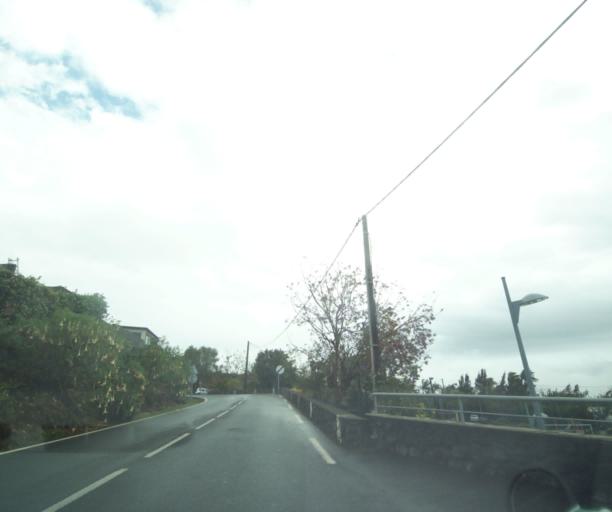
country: RE
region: Reunion
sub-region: Reunion
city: Saint-Paul
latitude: -21.0302
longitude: 55.2850
